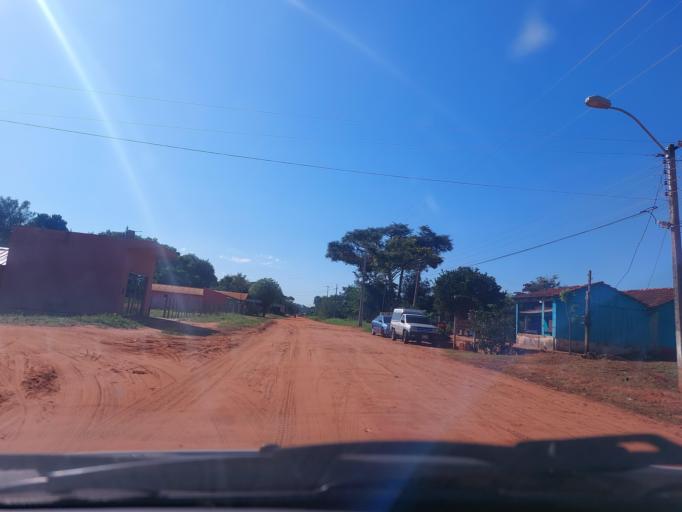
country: PY
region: San Pedro
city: Guayaybi
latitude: -24.5308
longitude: -56.3973
